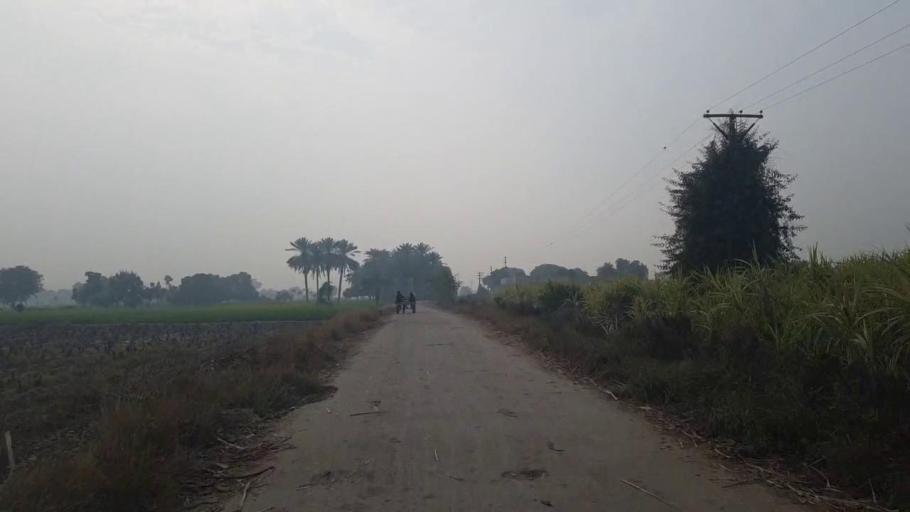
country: PK
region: Sindh
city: Tando Adam
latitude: 25.7163
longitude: 68.6804
